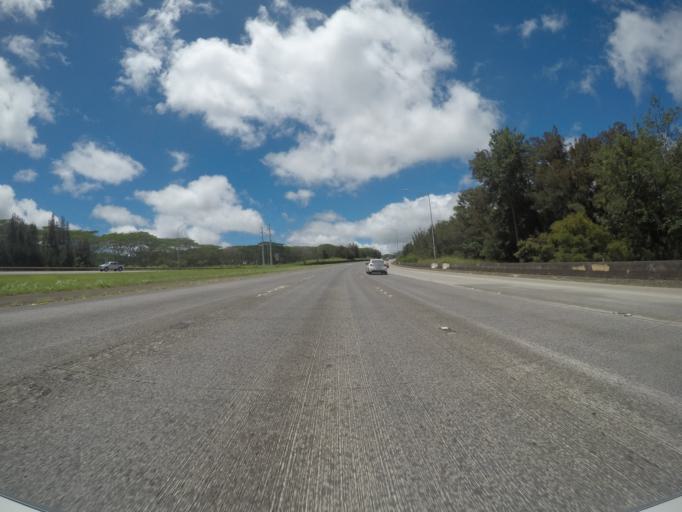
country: US
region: Hawaii
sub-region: Honolulu County
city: Mililani Town
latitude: 21.4416
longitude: -157.9935
